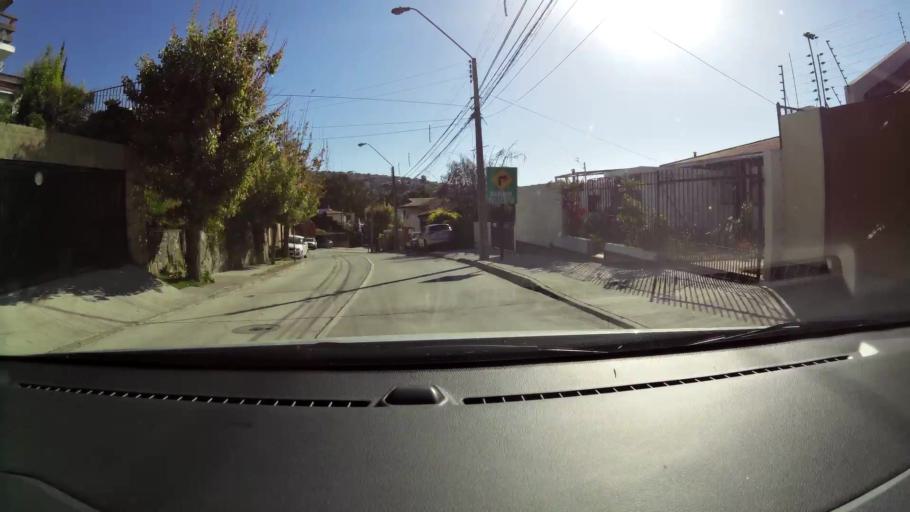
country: CL
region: Valparaiso
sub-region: Provincia de Valparaiso
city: Vina del Mar
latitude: -33.0354
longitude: -71.5583
